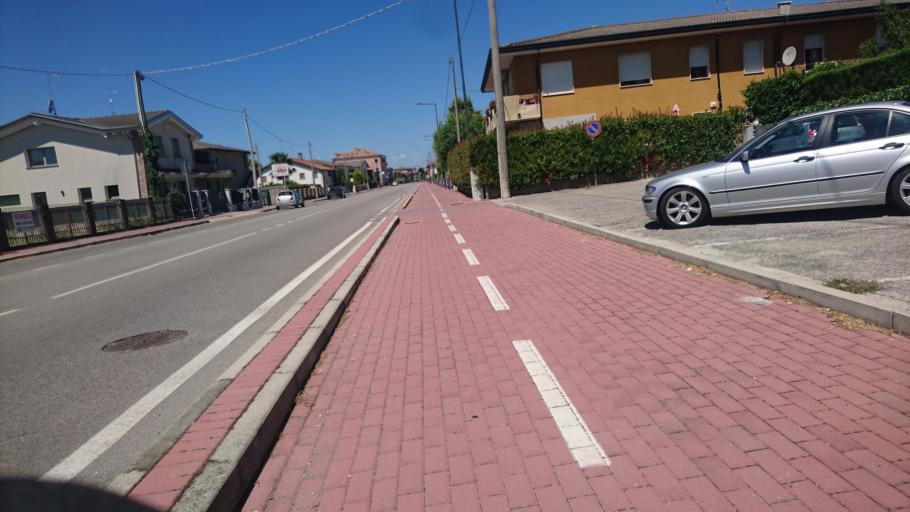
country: IT
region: Veneto
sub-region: Provincia di Padova
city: Campagnola
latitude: 45.2763
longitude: 12.0056
